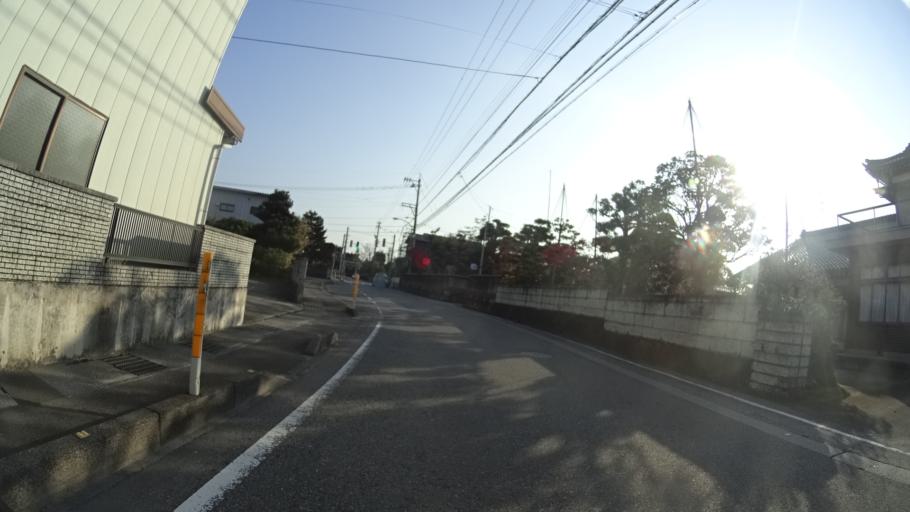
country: JP
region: Toyama
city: Toyama-shi
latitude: 36.6872
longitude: 137.2710
